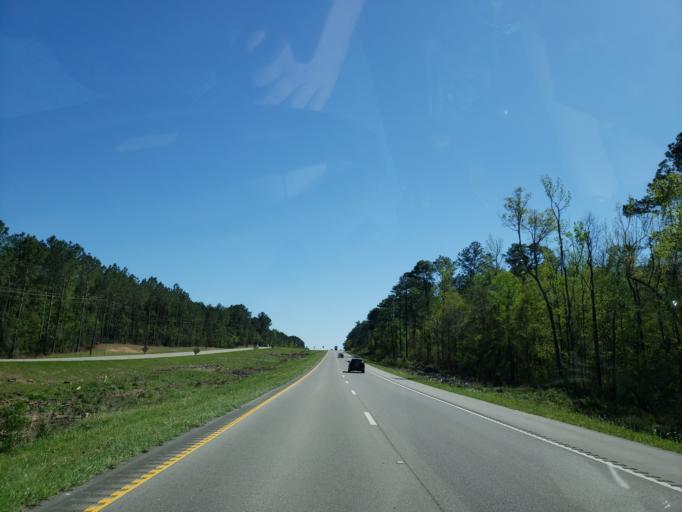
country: US
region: Mississippi
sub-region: Stone County
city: Wiggins
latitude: 31.0331
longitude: -89.2024
